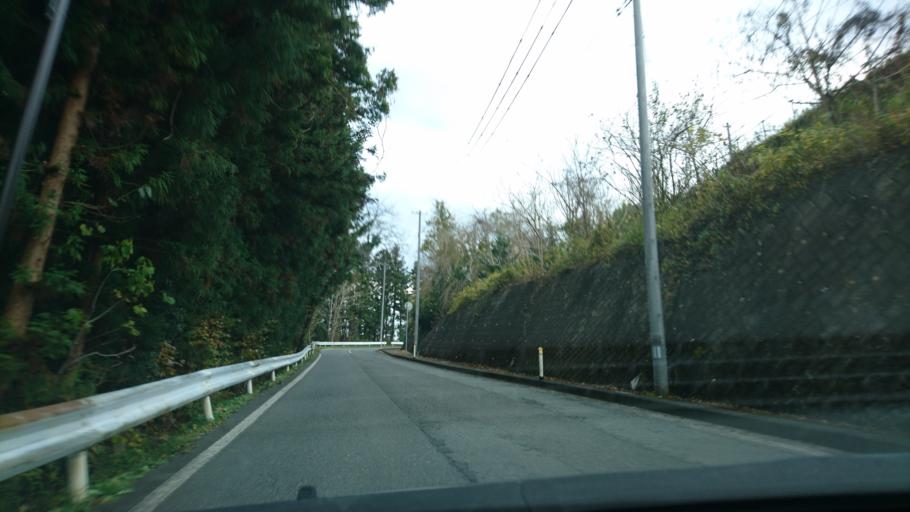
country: JP
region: Iwate
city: Ichinoseki
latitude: 38.9952
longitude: 141.2500
